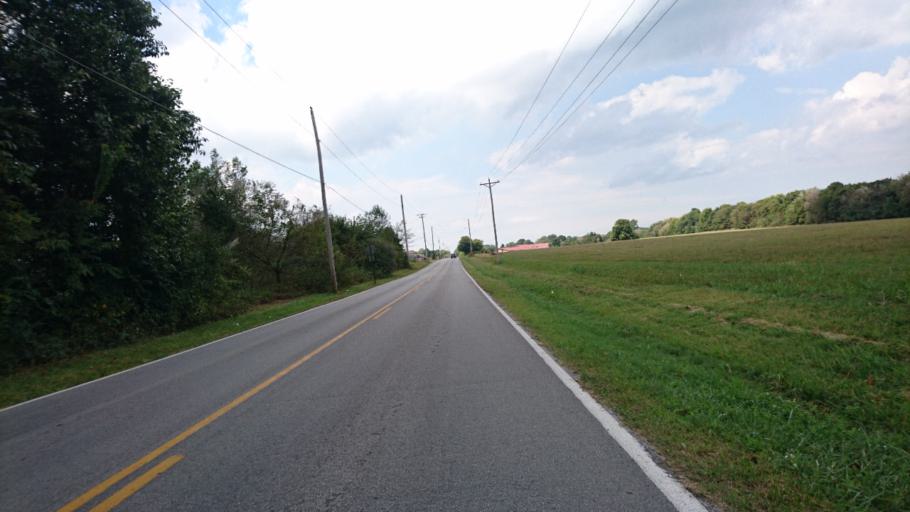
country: US
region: Missouri
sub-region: Greene County
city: Springfield
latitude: 37.1977
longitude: -93.3642
